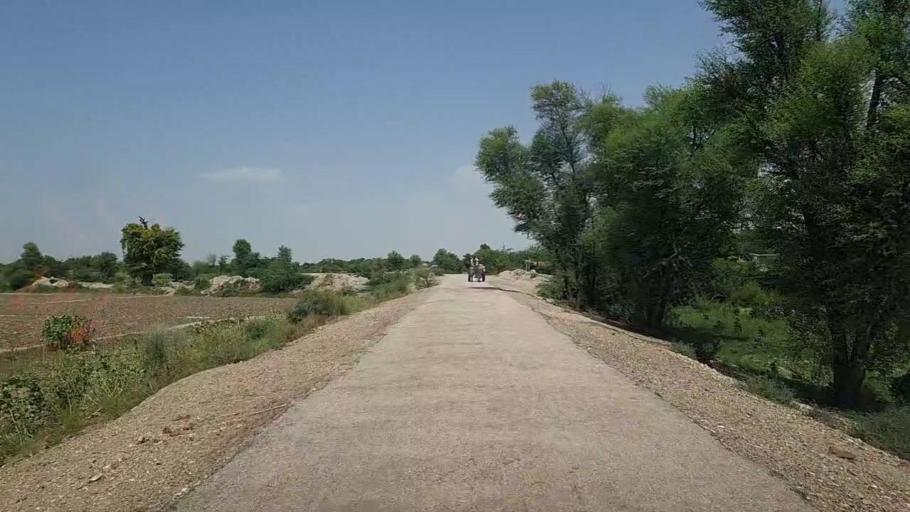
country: PK
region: Sindh
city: Pad Idan
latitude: 26.7870
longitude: 68.3473
